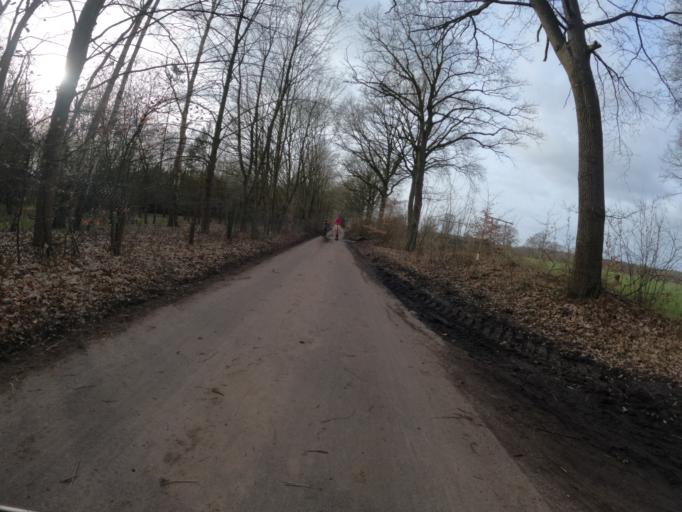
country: DE
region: Schleswig-Holstein
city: Appen
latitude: 53.6092
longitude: 9.7647
